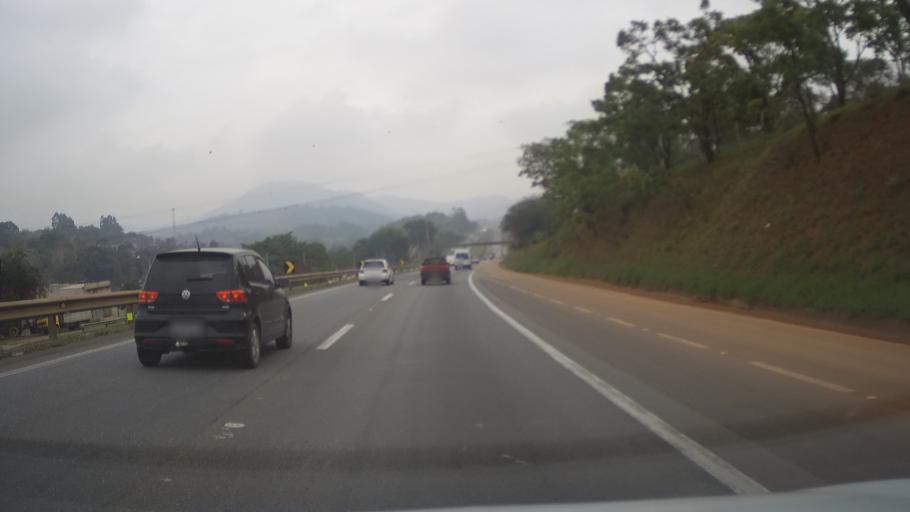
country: BR
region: Sao Paulo
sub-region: Atibaia
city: Atibaia
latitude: -23.0560
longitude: -46.5704
